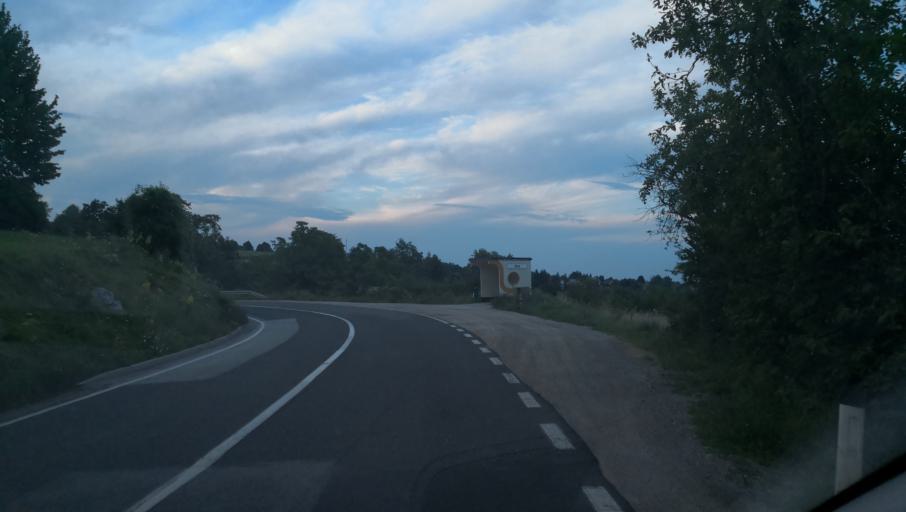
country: SI
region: Metlika
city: Metlika
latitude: 45.7009
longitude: 15.2536
